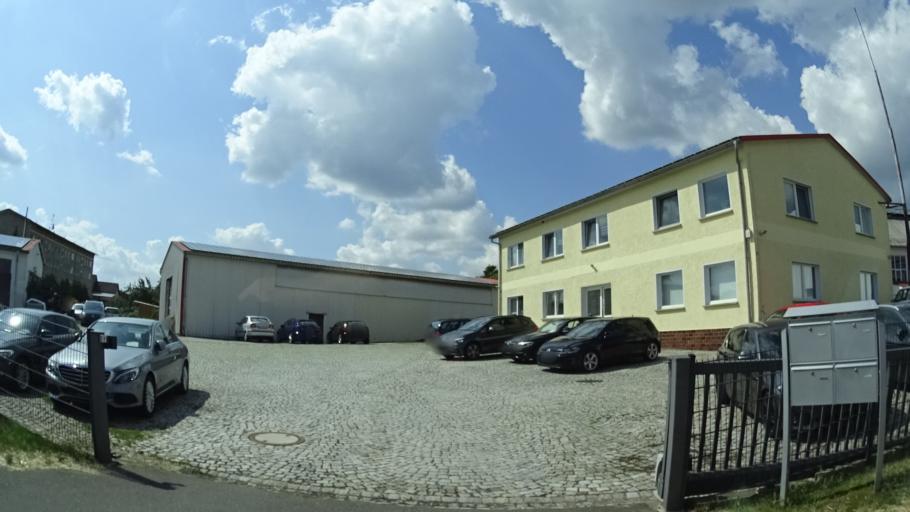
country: DE
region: Thuringia
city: Westhausen
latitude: 50.3603
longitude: 10.6879
